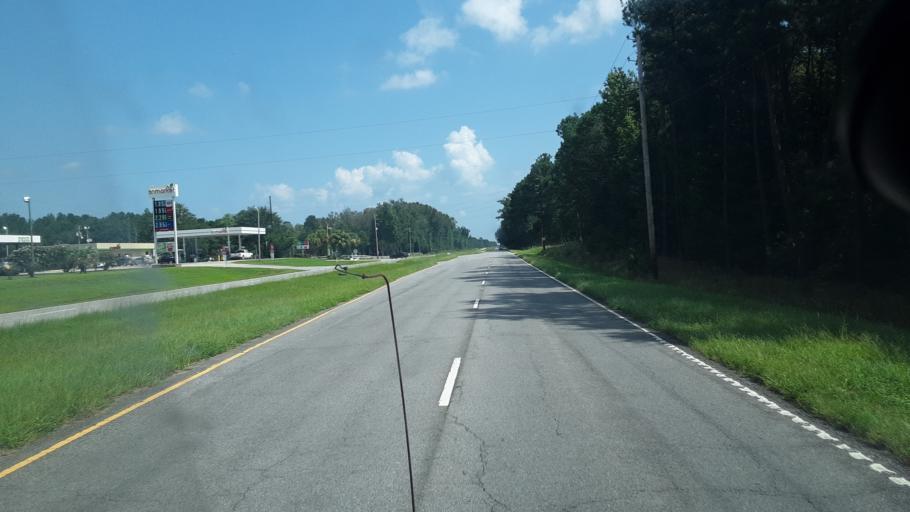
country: US
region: South Carolina
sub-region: Bamberg County
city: Bamberg
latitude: 33.3530
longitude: -81.0117
